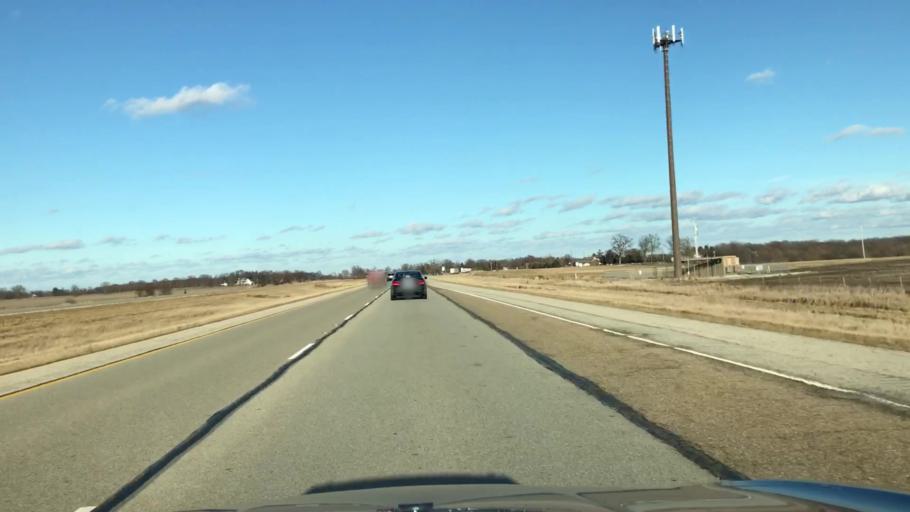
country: US
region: Illinois
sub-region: McLean County
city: Hudson
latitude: 40.5755
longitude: -88.8966
